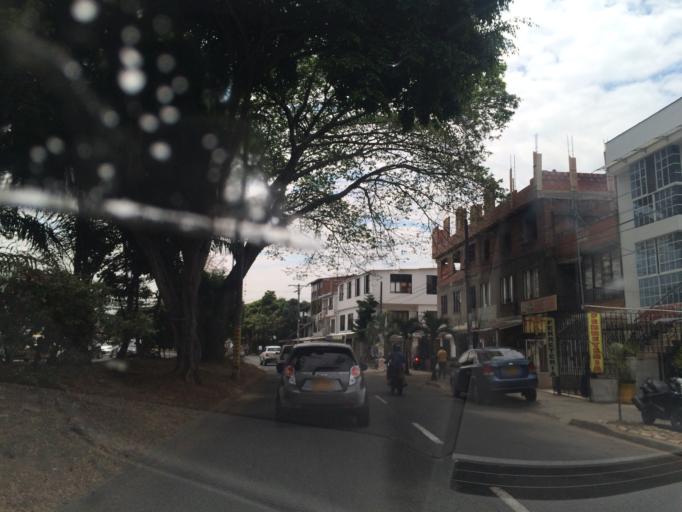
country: CO
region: Valle del Cauca
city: Cali
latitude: 3.4142
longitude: -76.5245
